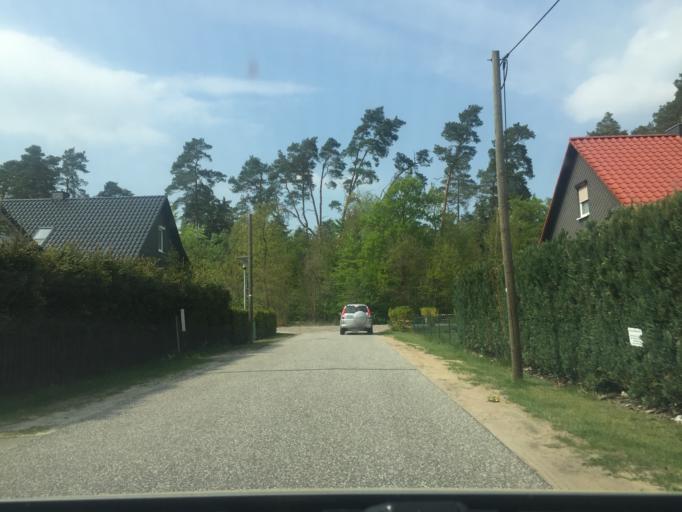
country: DE
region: Mecklenburg-Vorpommern
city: Torgelow
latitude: 53.6200
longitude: 14.0388
